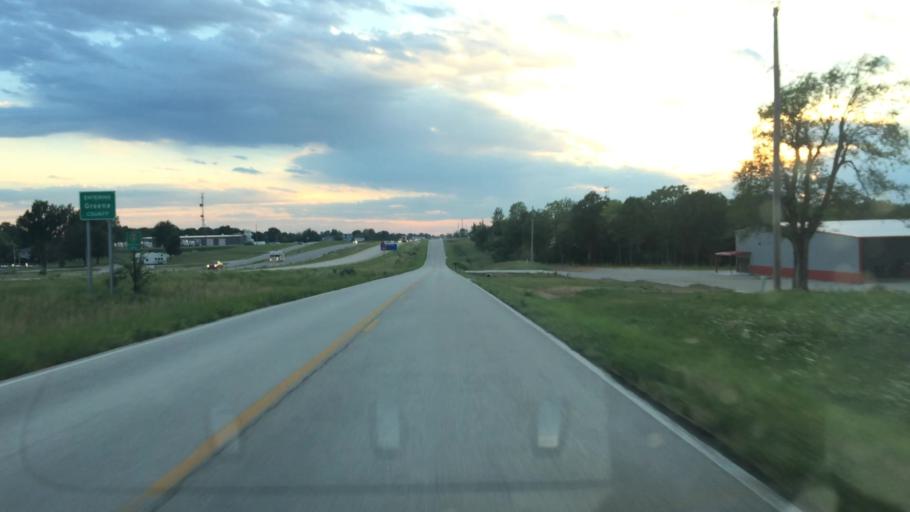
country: US
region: Missouri
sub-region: Greene County
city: Strafford
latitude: 37.2709
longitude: -93.0770
